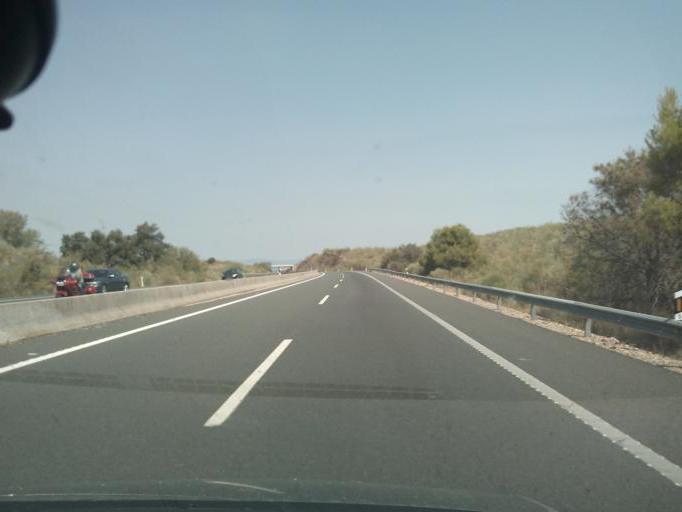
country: ES
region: Extremadura
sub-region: Provincia de Caceres
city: Casas de Miravete
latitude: 39.7399
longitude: -5.7246
